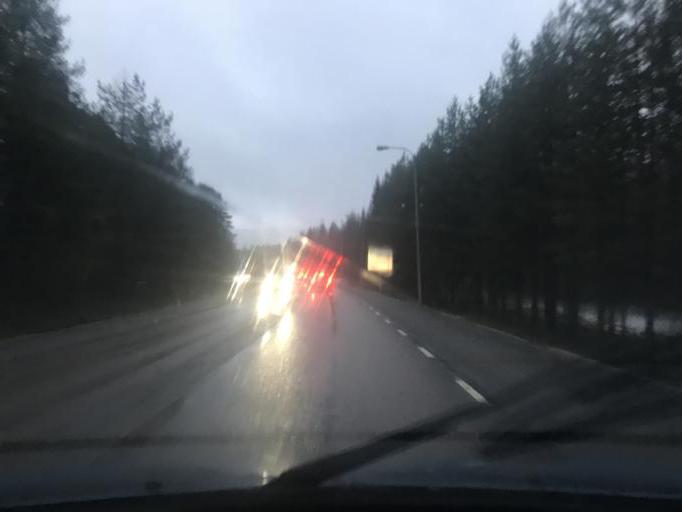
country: SE
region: Norrbotten
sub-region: Lulea Kommun
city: Gammelstad
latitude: 65.6202
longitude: 22.0358
